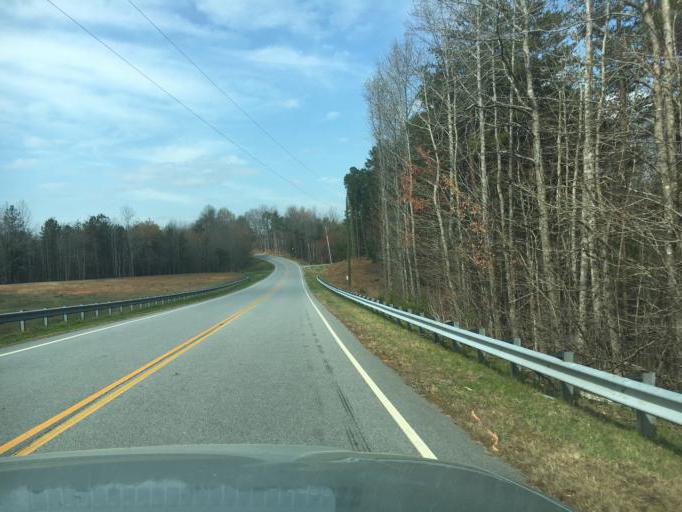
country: US
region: North Carolina
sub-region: Polk County
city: Tryon
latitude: 35.1257
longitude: -82.2703
